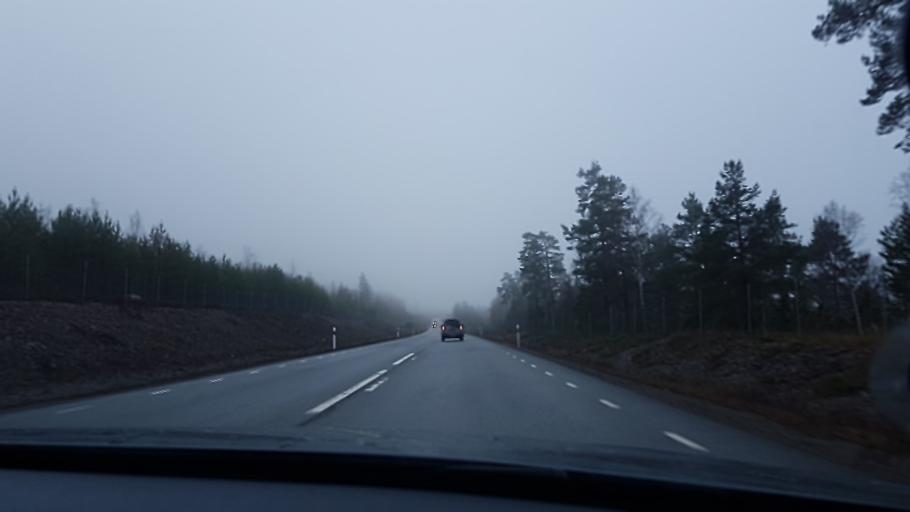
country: SE
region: Vaestra Goetaland
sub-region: Gullspangs Kommun
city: Gullspang
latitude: 58.8873
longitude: 14.0140
